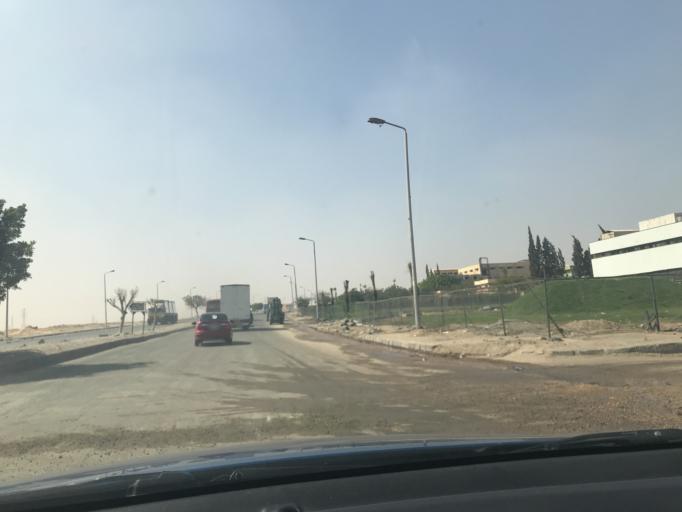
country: EG
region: Eastern Province
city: Bilbays
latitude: 30.2565
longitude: 31.7572
